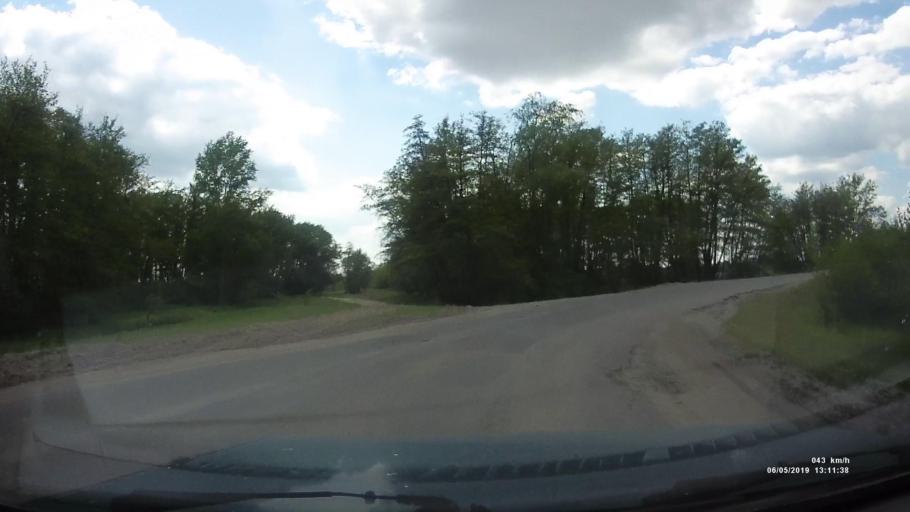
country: RU
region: Rostov
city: Ust'-Donetskiy
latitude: 47.7540
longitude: 40.9566
